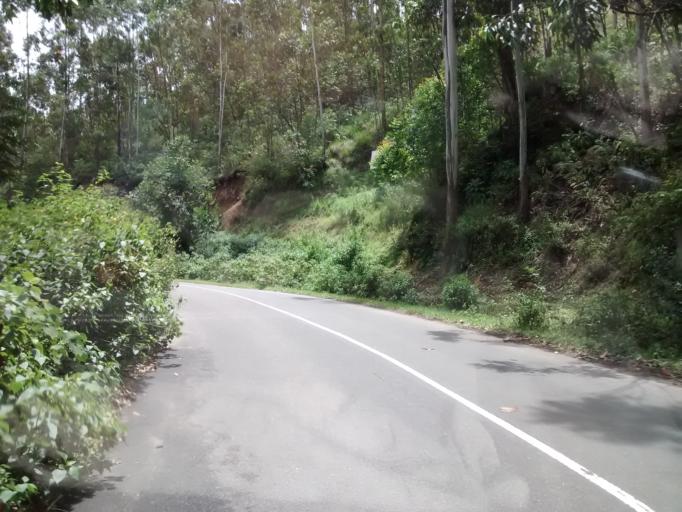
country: IN
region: Kerala
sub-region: Idukki
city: Munnar
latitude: 10.1285
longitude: 77.1653
